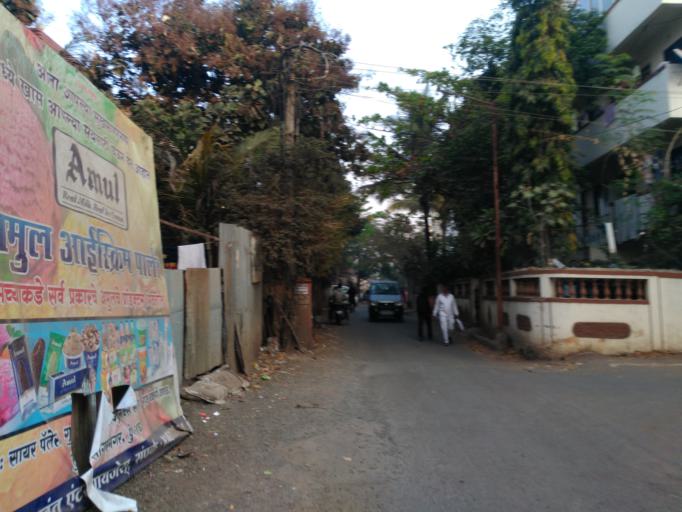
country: IN
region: Maharashtra
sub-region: Pune Division
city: Pune
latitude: 18.4563
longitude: 73.8732
